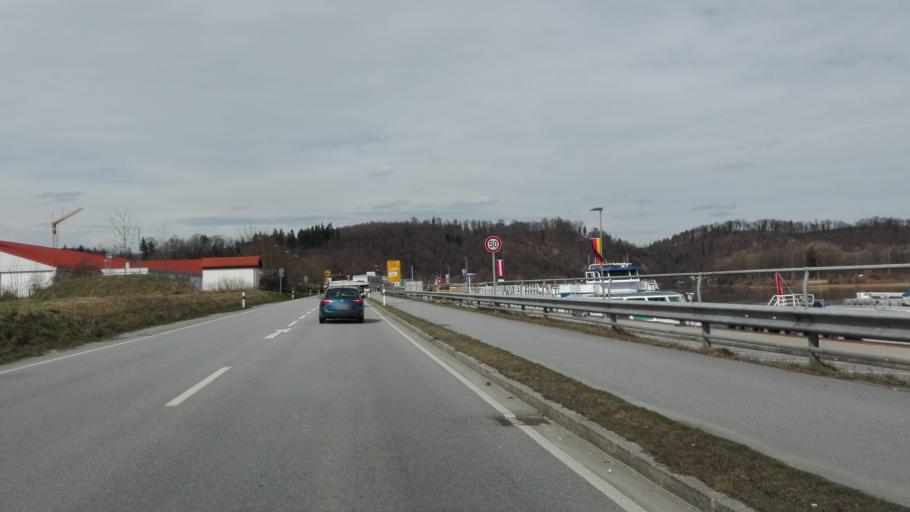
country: DE
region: Bavaria
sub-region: Lower Bavaria
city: Salzweg
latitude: 48.5828
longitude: 13.5002
